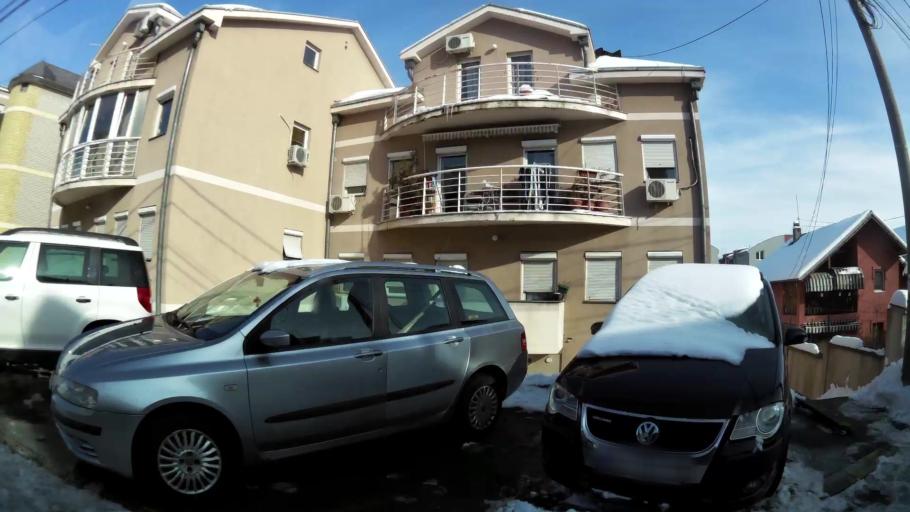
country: RS
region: Central Serbia
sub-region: Belgrade
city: Palilula
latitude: 44.8004
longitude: 20.5249
